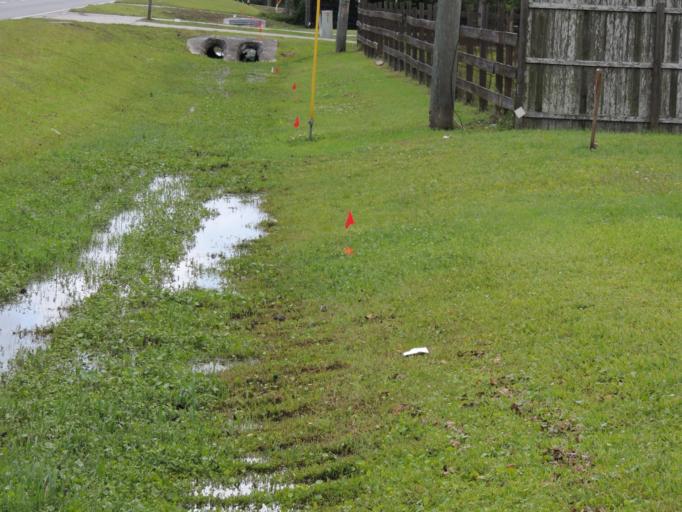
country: US
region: Florida
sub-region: Osceola County
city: Campbell
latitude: 28.2542
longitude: -81.4365
